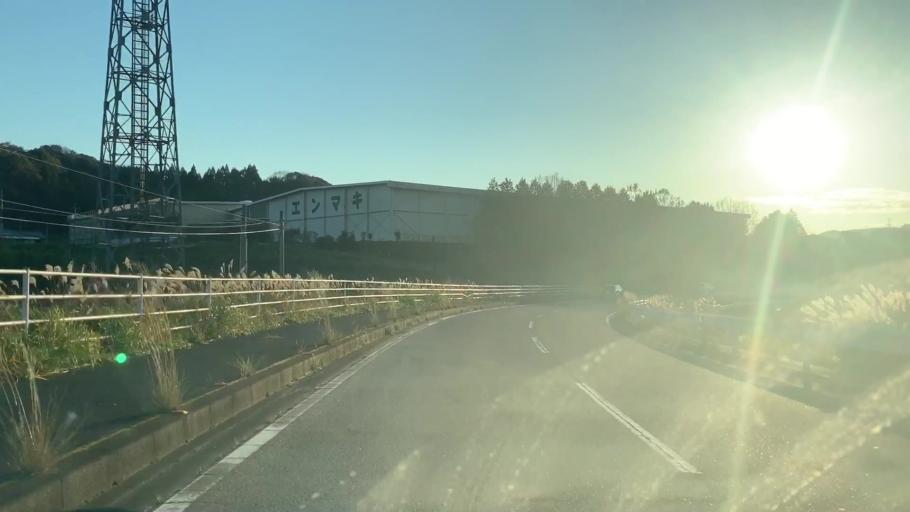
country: JP
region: Saga Prefecture
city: Karatsu
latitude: 33.3522
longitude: 130.0010
